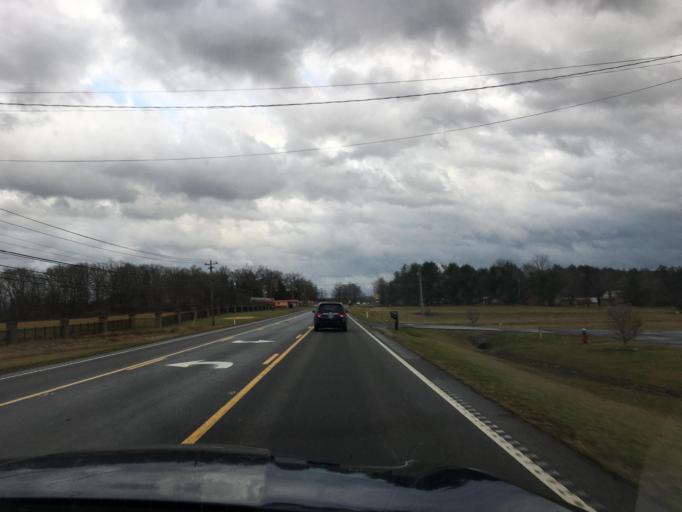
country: US
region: Tennessee
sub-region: Cumberland County
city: Crossville
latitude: 35.9251
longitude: -85.0039
